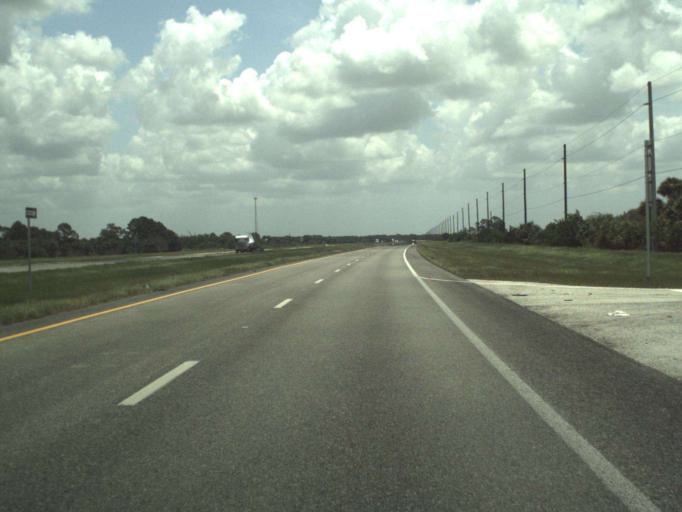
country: US
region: Florida
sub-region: Saint Lucie County
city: Fort Pierce South
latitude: 27.3708
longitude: -80.5930
